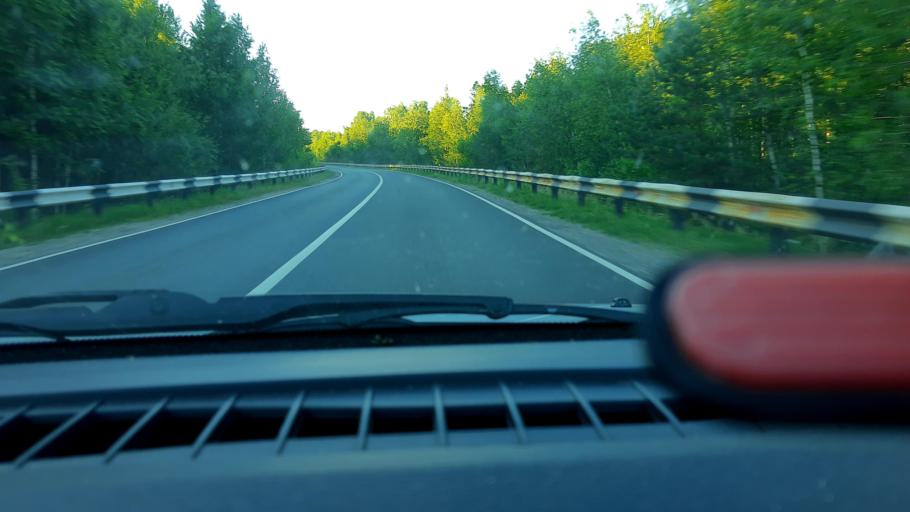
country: RU
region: Nizjnij Novgorod
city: Krasnyye Baki
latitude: 57.1180
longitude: 45.2090
